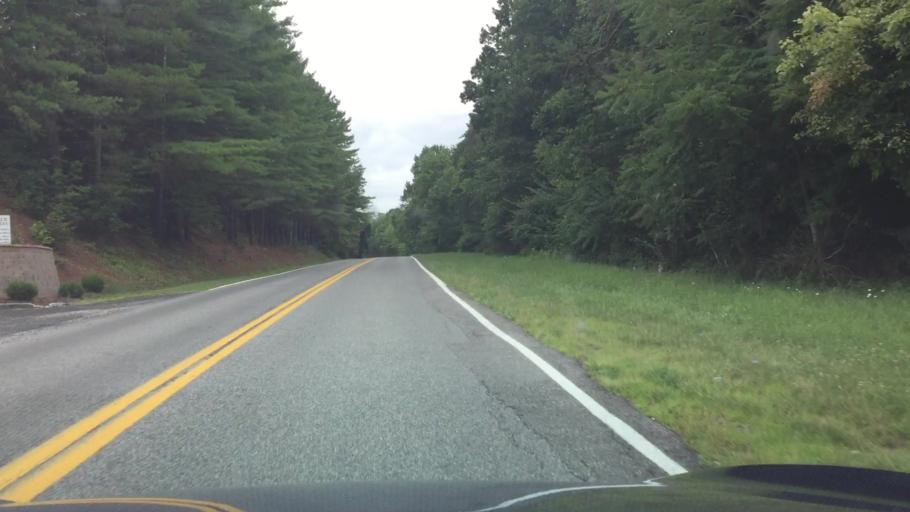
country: US
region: Virginia
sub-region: Pulaski County
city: Pulaski
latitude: 37.0205
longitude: -80.7306
